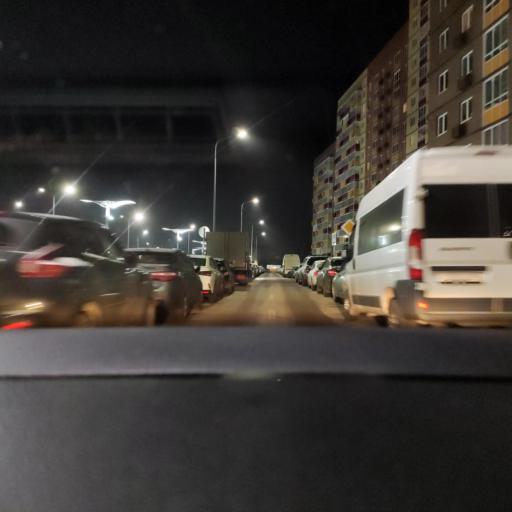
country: RU
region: Moskovskaya
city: Petrovskaya
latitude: 55.5599
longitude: 37.8106
